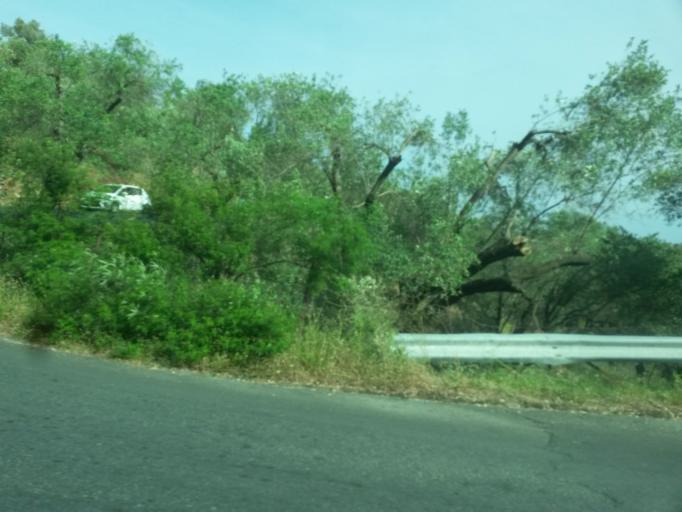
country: GR
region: North Aegean
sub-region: Nomos Lesvou
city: Palaiokipos
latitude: 39.0681
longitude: 26.4572
